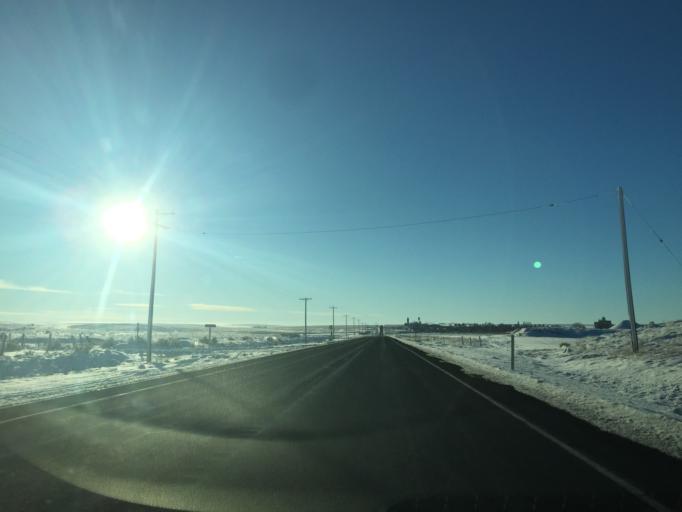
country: US
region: Washington
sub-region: Okanogan County
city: Coulee Dam
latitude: 47.7141
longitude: -118.9155
